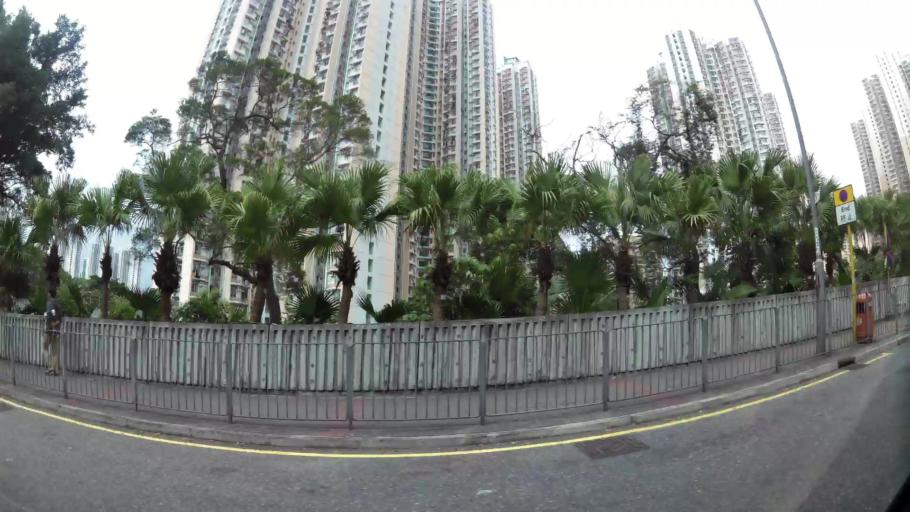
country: HK
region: Kowloon City
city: Kowloon
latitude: 22.3160
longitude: 114.2363
